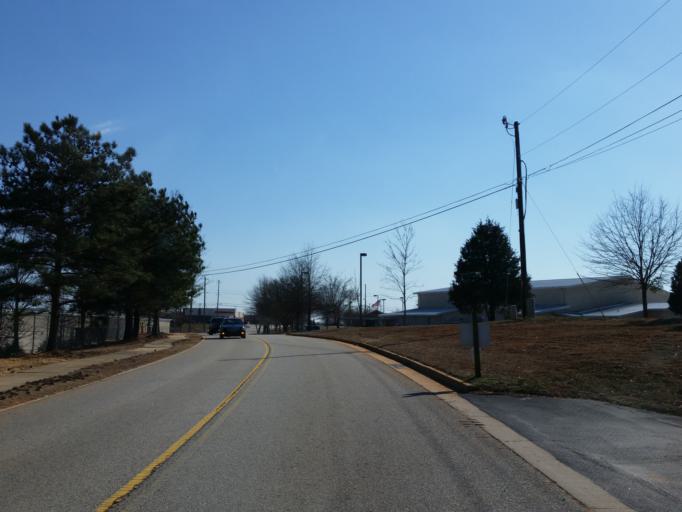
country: US
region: Georgia
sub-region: Henry County
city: McDonough
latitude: 33.4671
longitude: -84.2220
